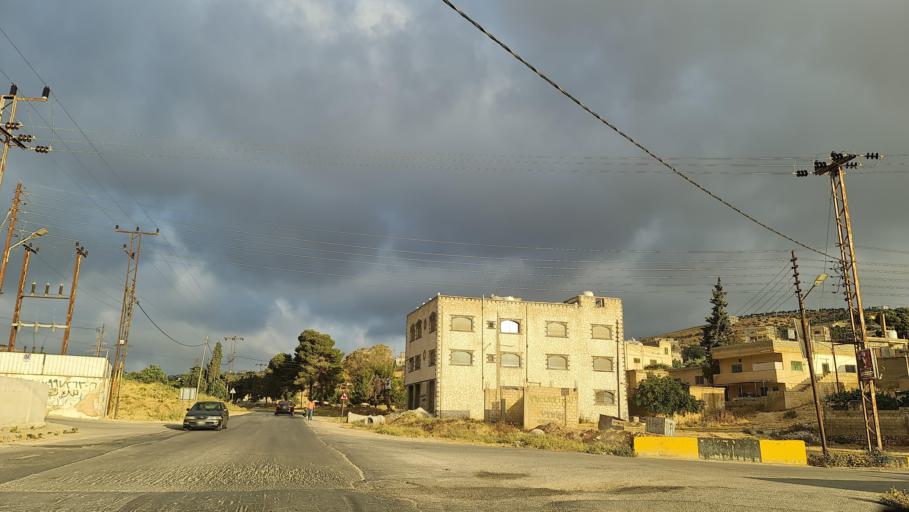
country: JO
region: Amman
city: Al Jubayhah
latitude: 32.0930
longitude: 35.9256
